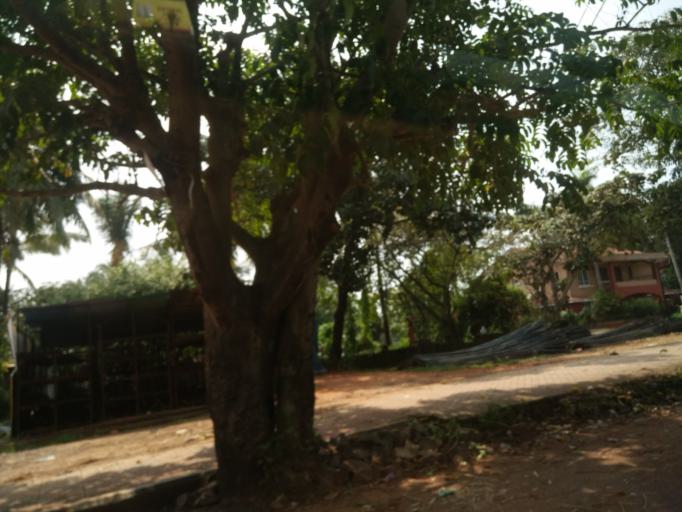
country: IN
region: Goa
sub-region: North Goa
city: Serula
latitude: 15.5323
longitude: 73.8237
